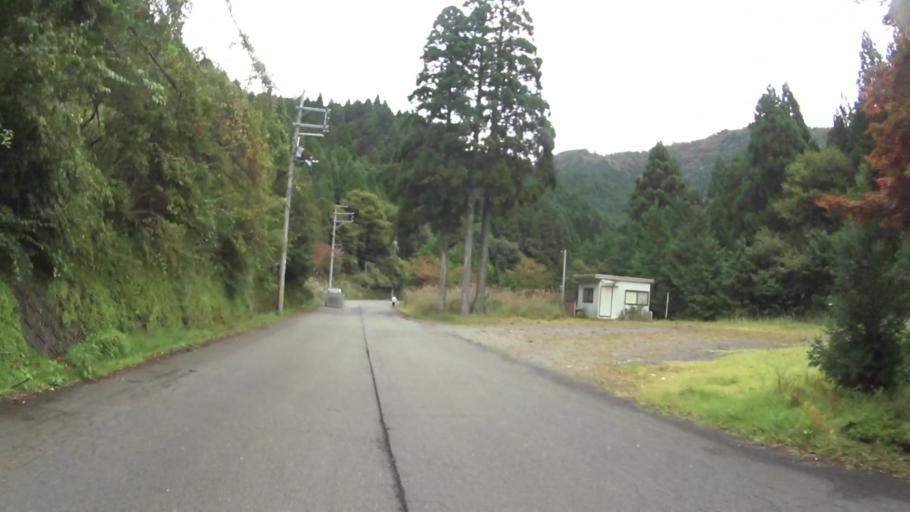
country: JP
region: Shiga Prefecture
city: Kitahama
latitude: 35.1799
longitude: 135.7834
